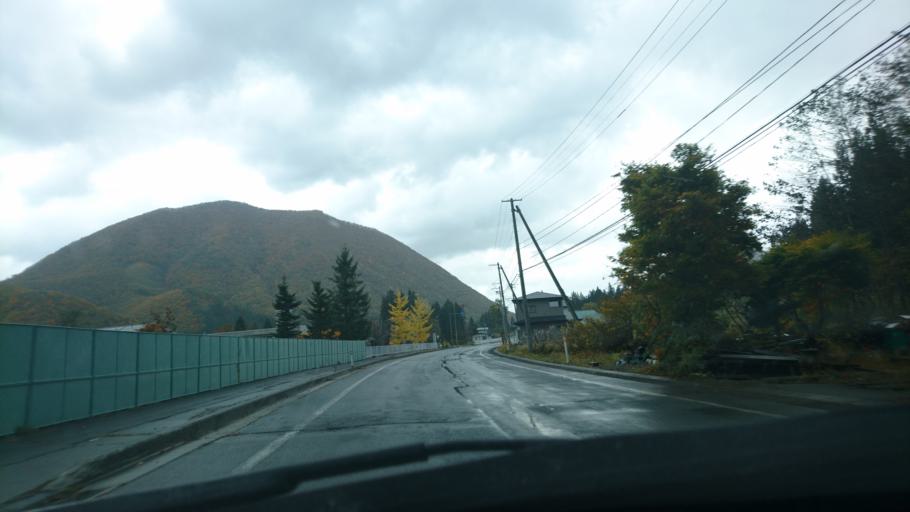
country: JP
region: Iwate
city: Shizukuishi
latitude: 39.5983
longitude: 140.9243
